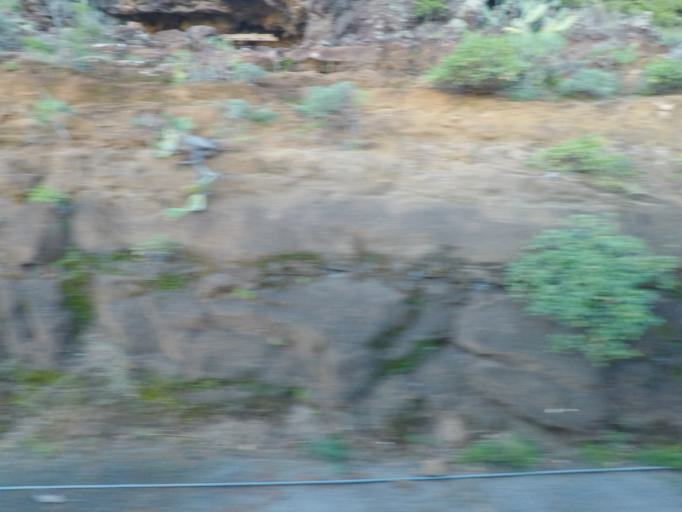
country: ES
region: Canary Islands
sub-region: Provincia de Santa Cruz de Tenerife
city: Alajero
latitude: 28.0658
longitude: -17.2048
